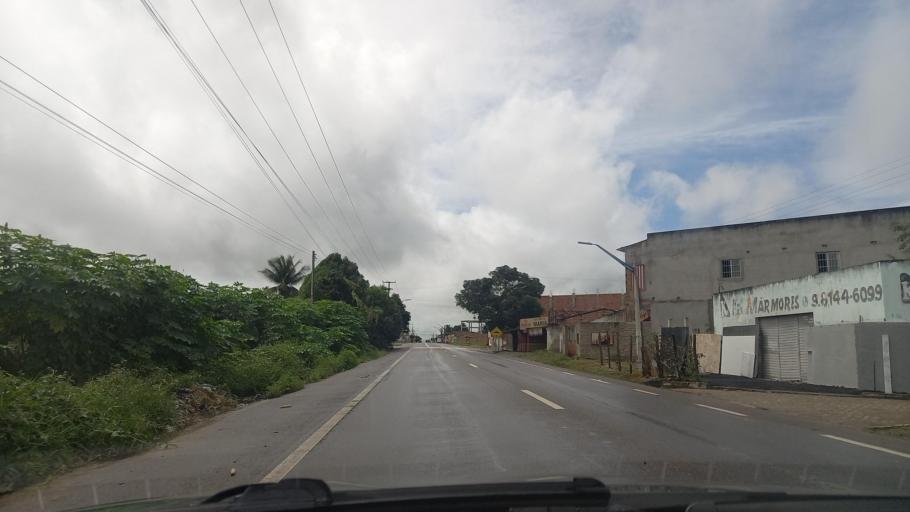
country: BR
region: Alagoas
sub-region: Limoeiro De Anadia
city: Limoeiro de Anadia
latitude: -9.7587
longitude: -36.5613
